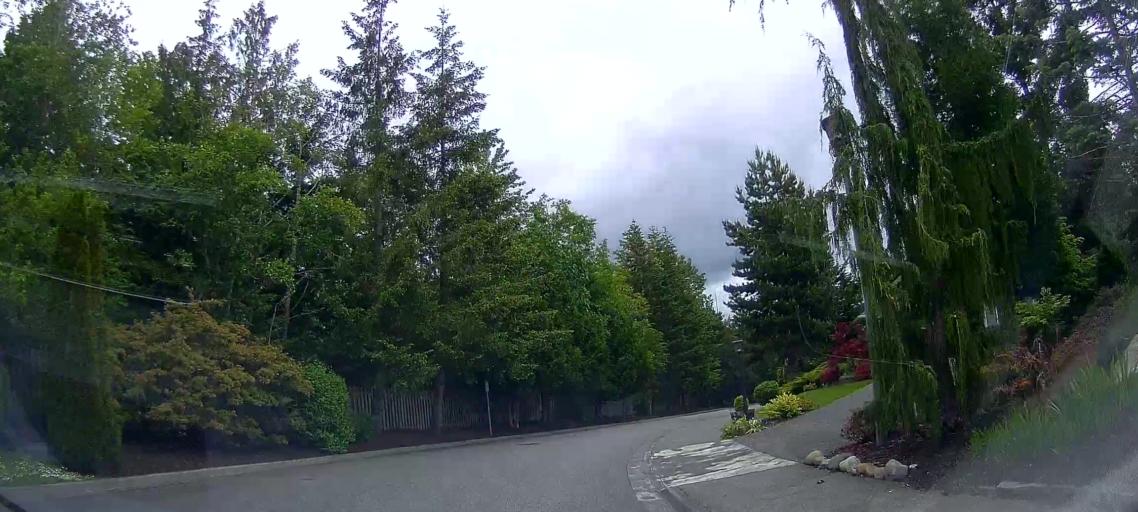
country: US
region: Washington
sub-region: Skagit County
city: Big Lake
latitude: 48.4134
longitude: -122.2844
